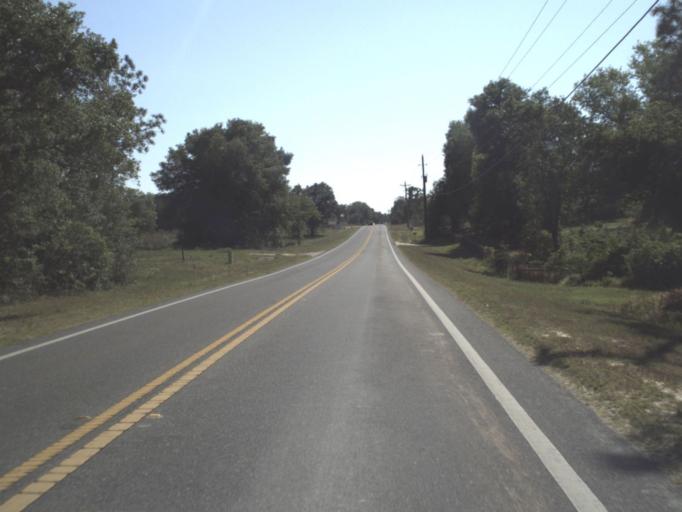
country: US
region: Florida
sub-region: Marion County
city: Dunnellon
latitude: 29.1344
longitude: -82.3983
